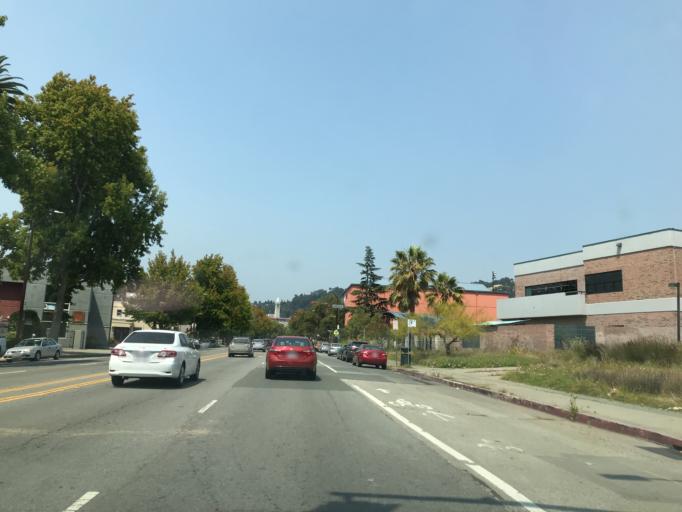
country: US
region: California
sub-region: Alameda County
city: Berkeley
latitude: 37.8596
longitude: -122.2592
